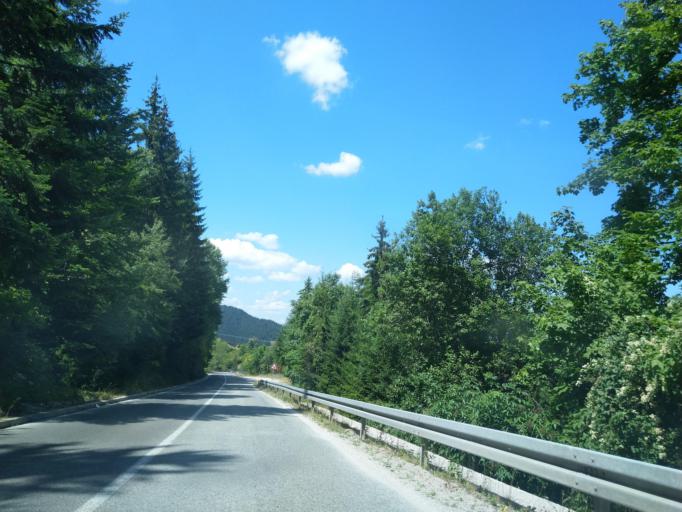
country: RS
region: Central Serbia
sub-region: Zlatiborski Okrug
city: Nova Varos
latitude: 43.4175
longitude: 19.8295
